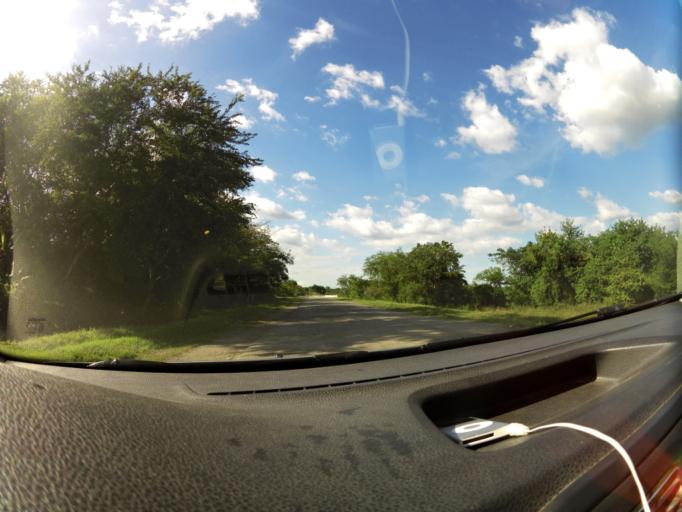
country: CU
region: Santiago de Cuba
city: Palma Soriano
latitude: 20.2515
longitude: -75.9826
